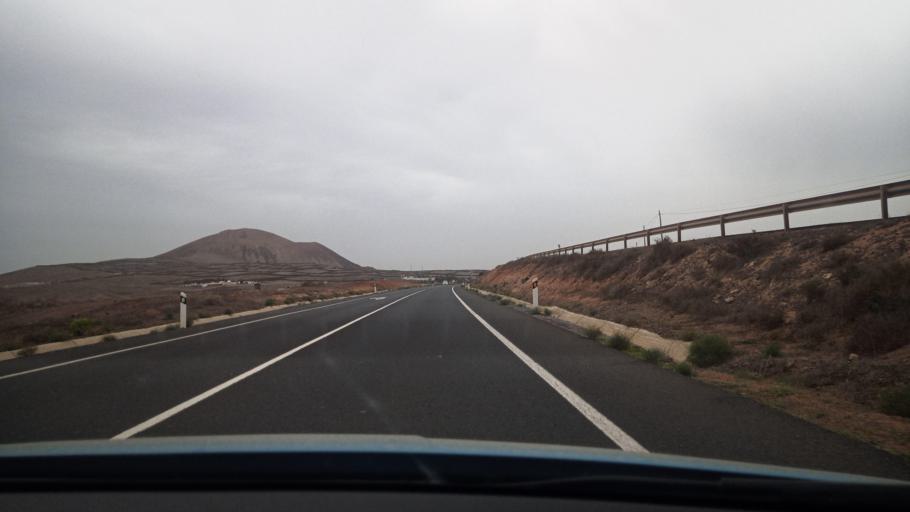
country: ES
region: Canary Islands
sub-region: Provincia de Las Palmas
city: Nazaret
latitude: 29.0285
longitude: -13.5257
